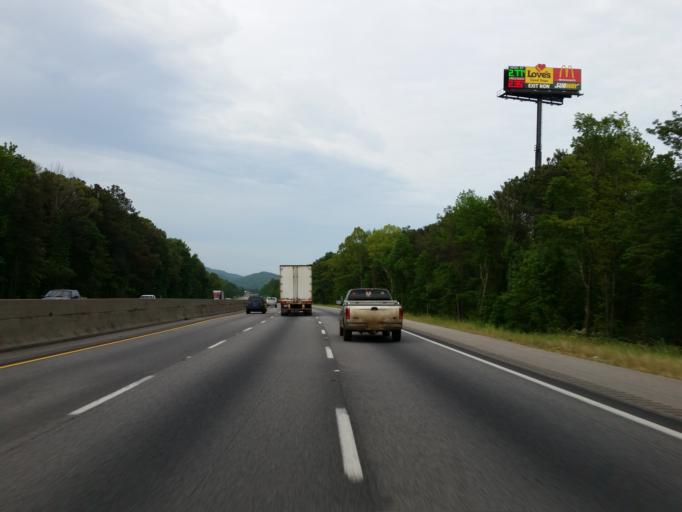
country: US
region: Alabama
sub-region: Saint Clair County
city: Moody
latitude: 33.5701
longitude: -86.4985
